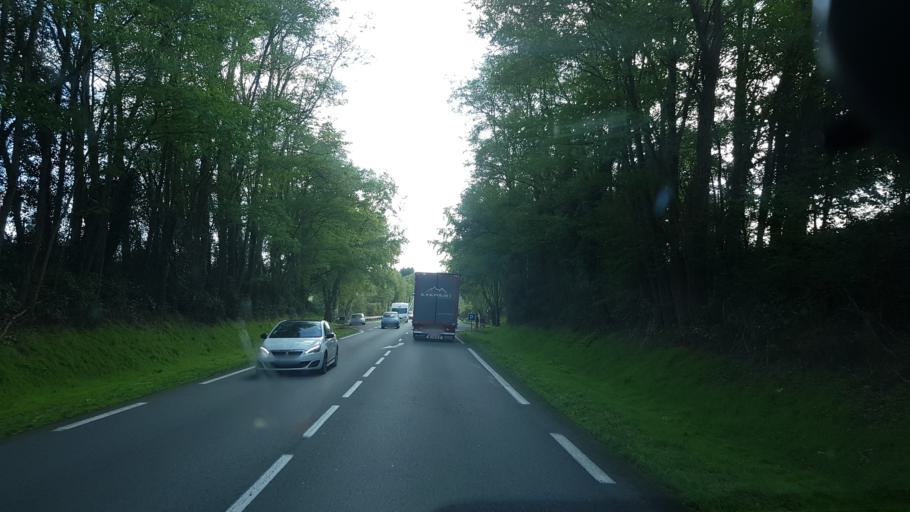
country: FR
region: Poitou-Charentes
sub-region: Departement de la Charente
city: Confolens
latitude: 46.0375
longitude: 0.6588
